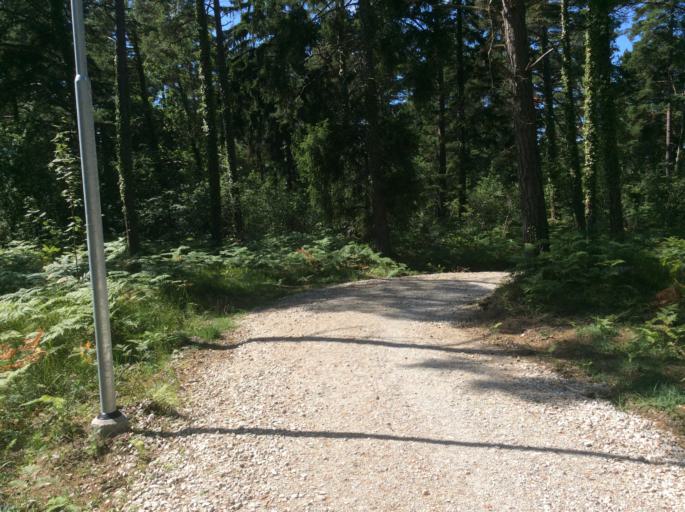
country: SE
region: Gotland
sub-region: Gotland
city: Vibble
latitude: 57.6014
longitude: 18.2753
